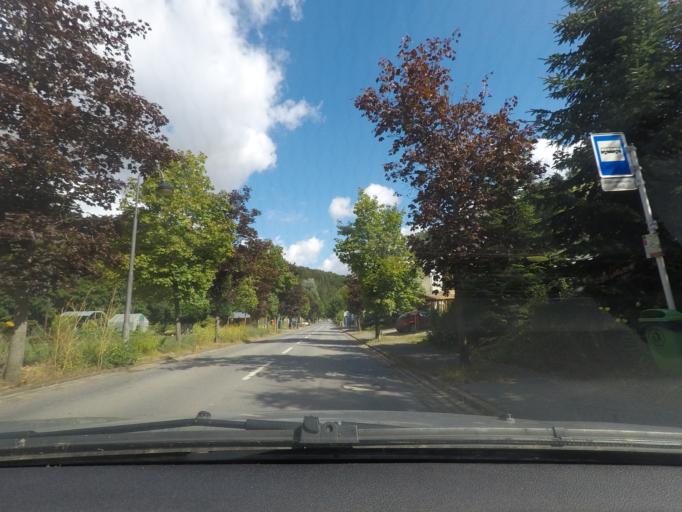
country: LU
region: Luxembourg
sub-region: Canton de Mersch
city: Heffingen
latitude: 49.7439
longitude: 6.2658
